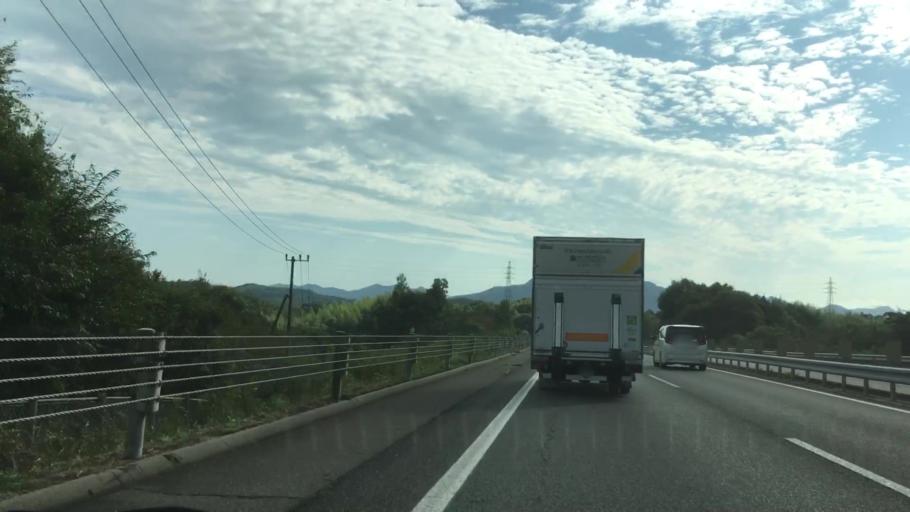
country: JP
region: Yamaguchi
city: Yanai
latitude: 34.0945
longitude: 132.0972
